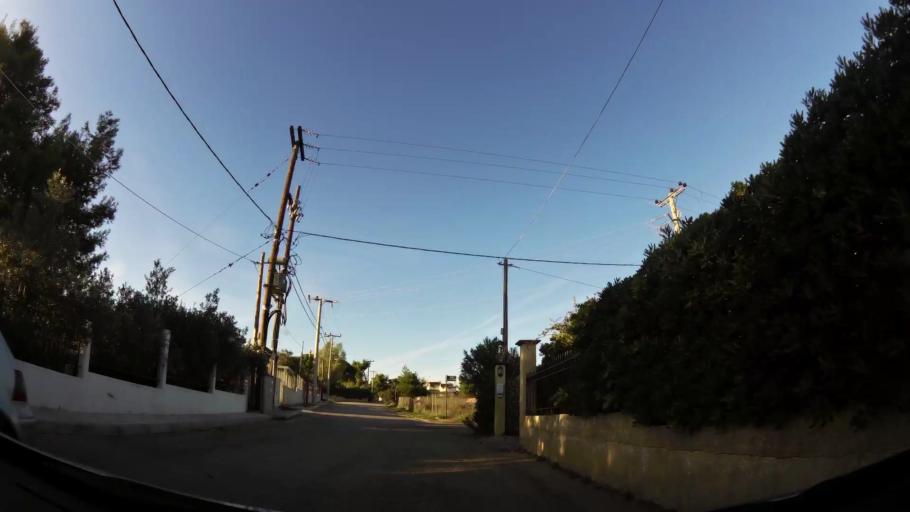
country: GR
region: Attica
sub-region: Nomarchia Anatolikis Attikis
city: Kryoneri
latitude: 38.1292
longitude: 23.8253
